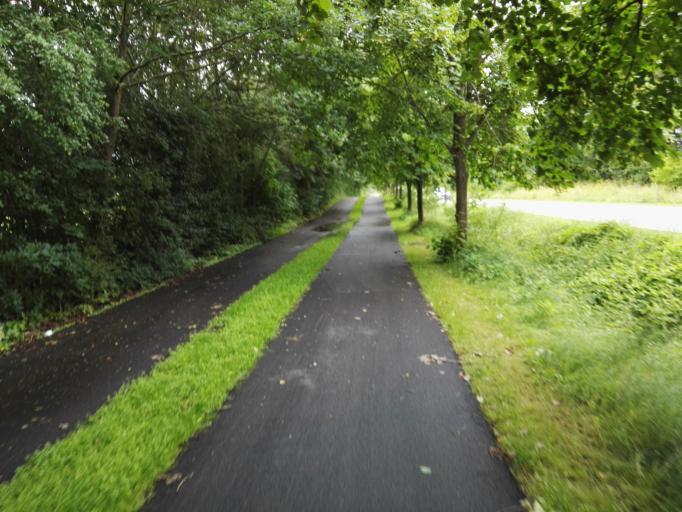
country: DK
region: Capital Region
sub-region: Egedal Kommune
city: Olstykke
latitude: 55.7788
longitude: 12.1602
